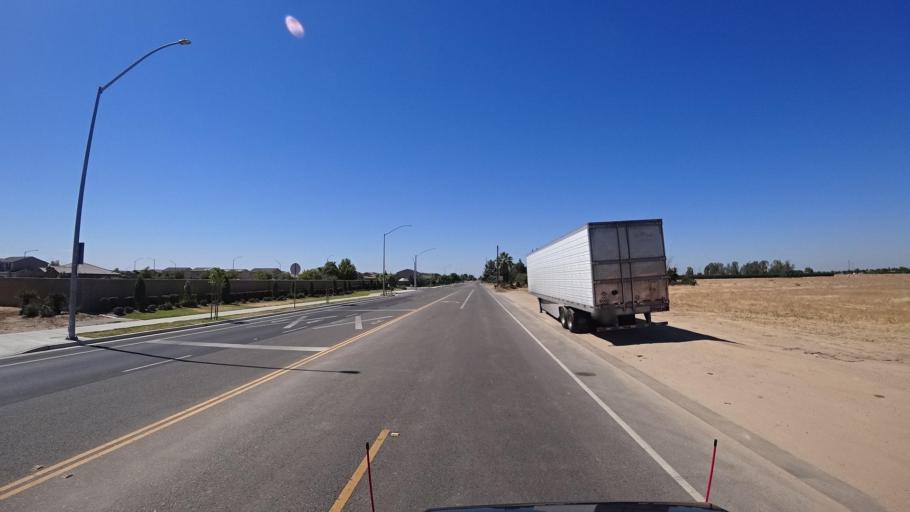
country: US
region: California
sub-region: Fresno County
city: Sunnyside
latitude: 36.7215
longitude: -119.6731
